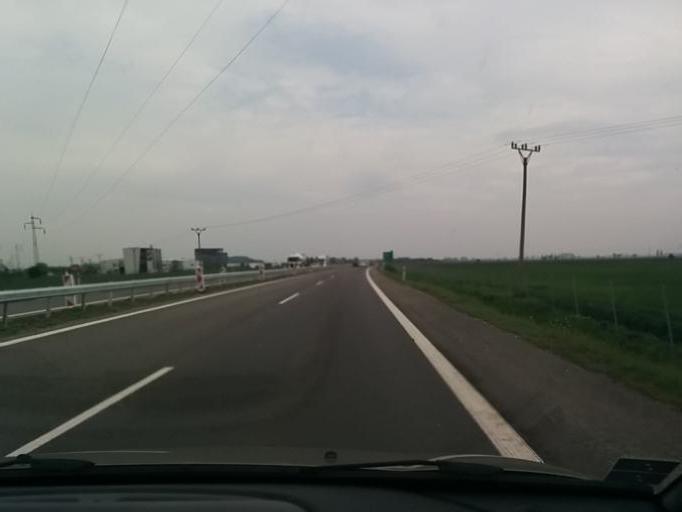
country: SK
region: Trnavsky
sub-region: Okres Galanta
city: Galanta
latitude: 48.2792
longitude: 17.7128
